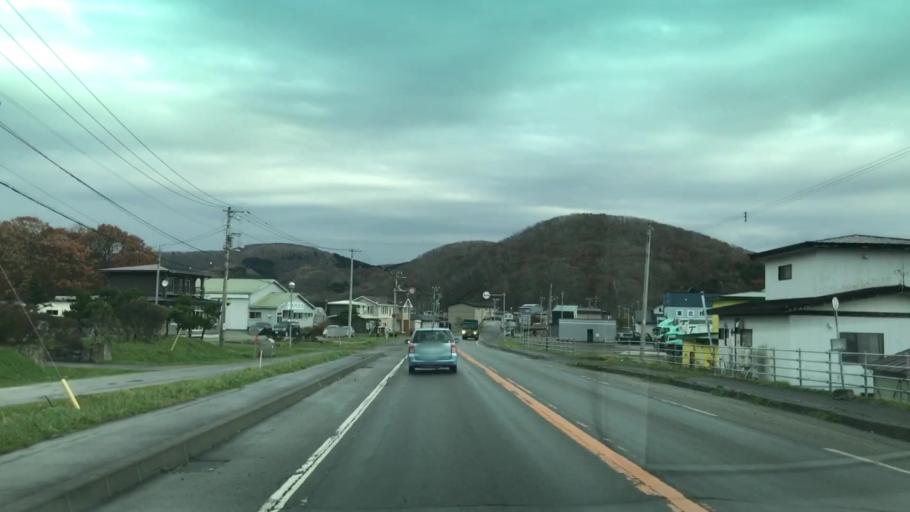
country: JP
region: Hokkaido
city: Shizunai-furukawacho
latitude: 42.1336
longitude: 142.9046
